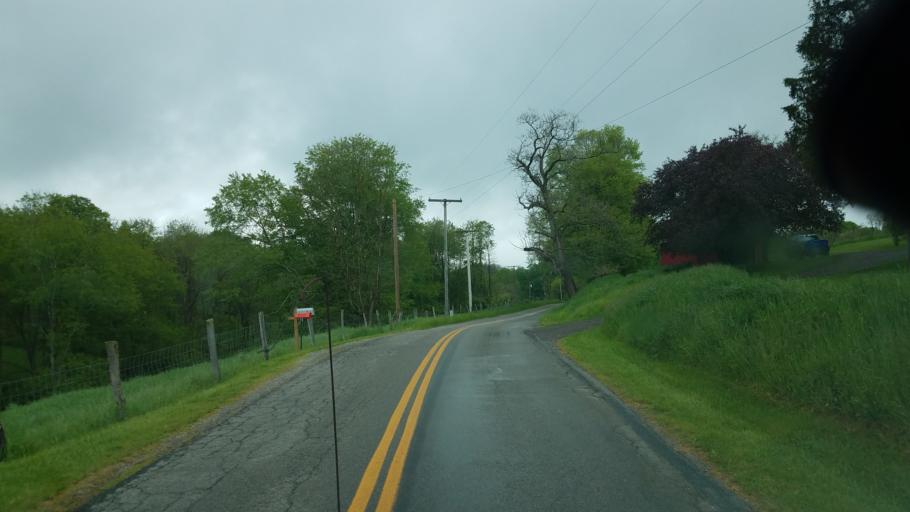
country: US
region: Ohio
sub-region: Harrison County
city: Cadiz
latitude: 40.2727
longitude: -80.8544
